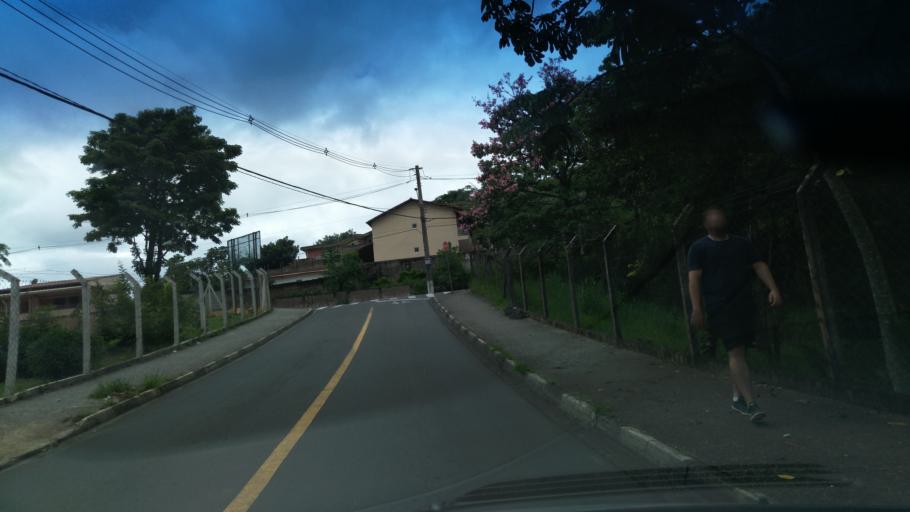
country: BR
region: Sao Paulo
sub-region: Valinhos
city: Valinhos
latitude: -22.9579
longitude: -46.9799
